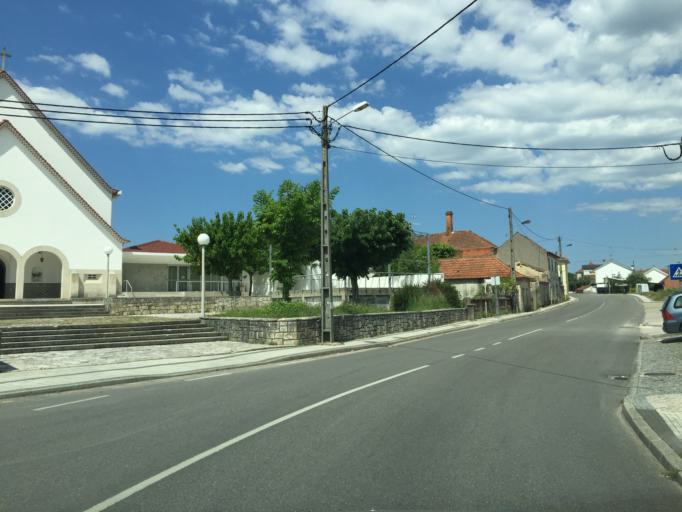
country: PT
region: Santarem
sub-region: Ourem
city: Ourem
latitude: 39.7117
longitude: -8.5303
